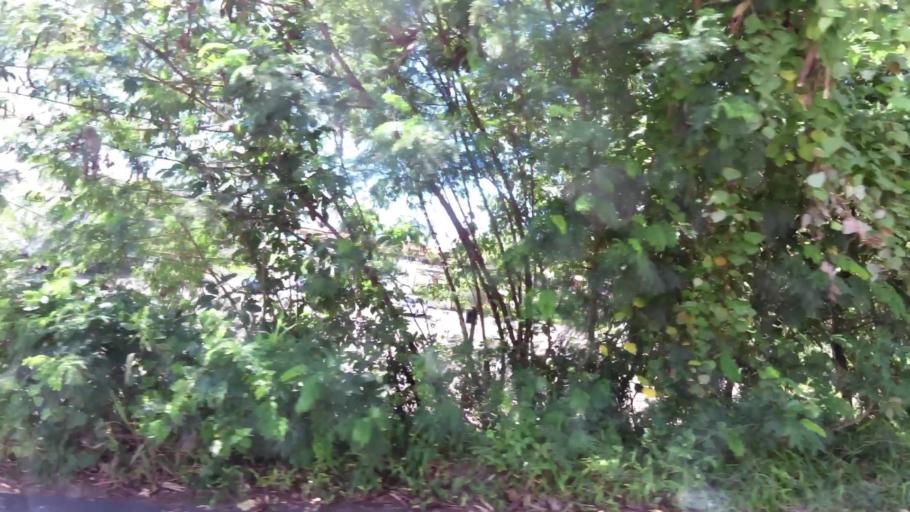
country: BN
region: Brunei and Muara
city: Bandar Seri Begawan
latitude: 4.9675
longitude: 114.9473
